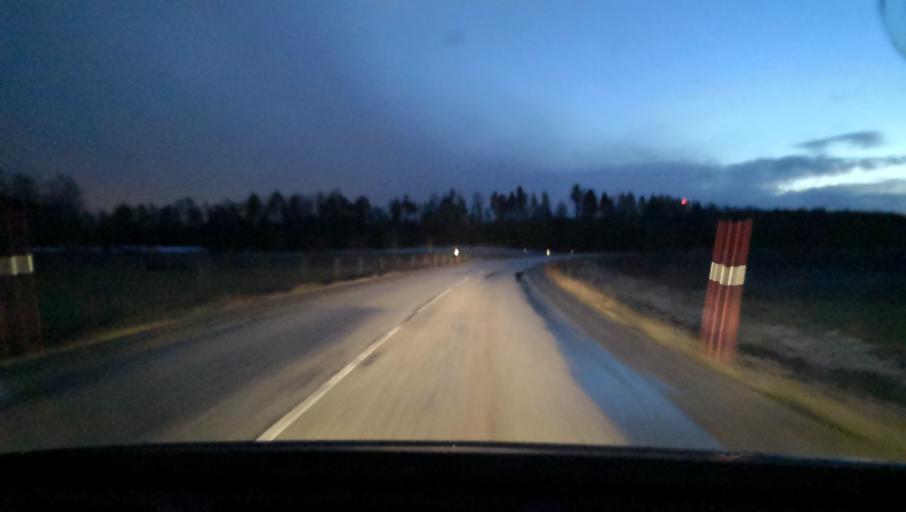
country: SE
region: Vaestmanland
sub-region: Vasteras
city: Skultuna
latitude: 59.7429
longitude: 16.4548
